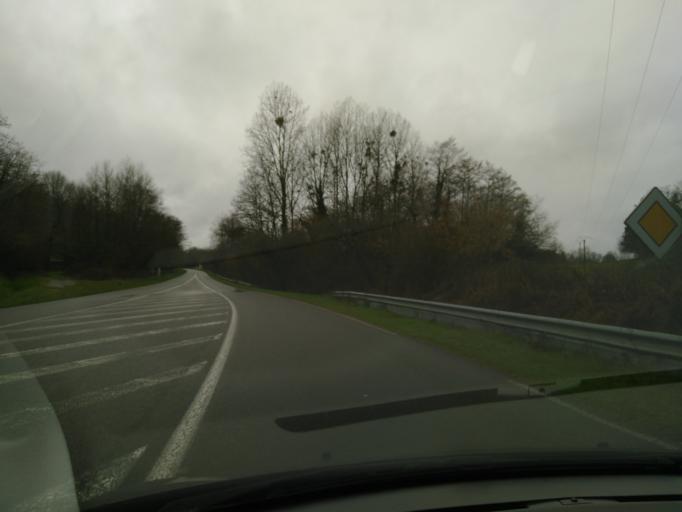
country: FR
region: Limousin
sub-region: Departement de la Haute-Vienne
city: Le Vigen
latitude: 45.7392
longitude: 1.2811
